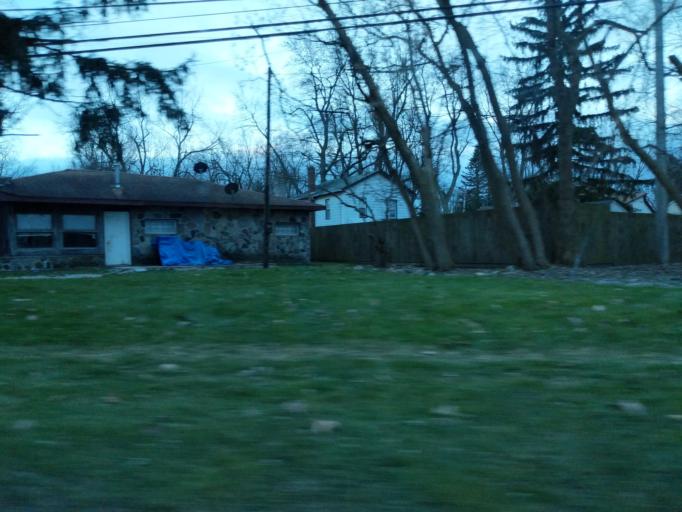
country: US
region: Michigan
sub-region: Lapeer County
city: Almont
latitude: 42.9267
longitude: -83.0469
